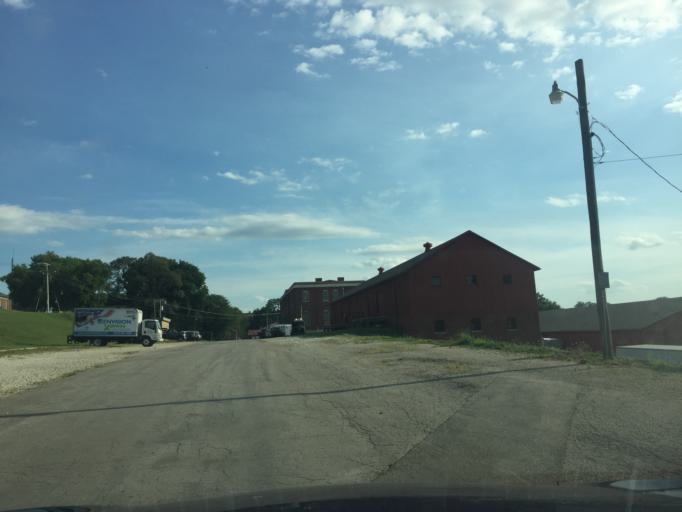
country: US
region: Kansas
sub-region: Leavenworth County
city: Leavenworth
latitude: 39.3600
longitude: -94.9206
